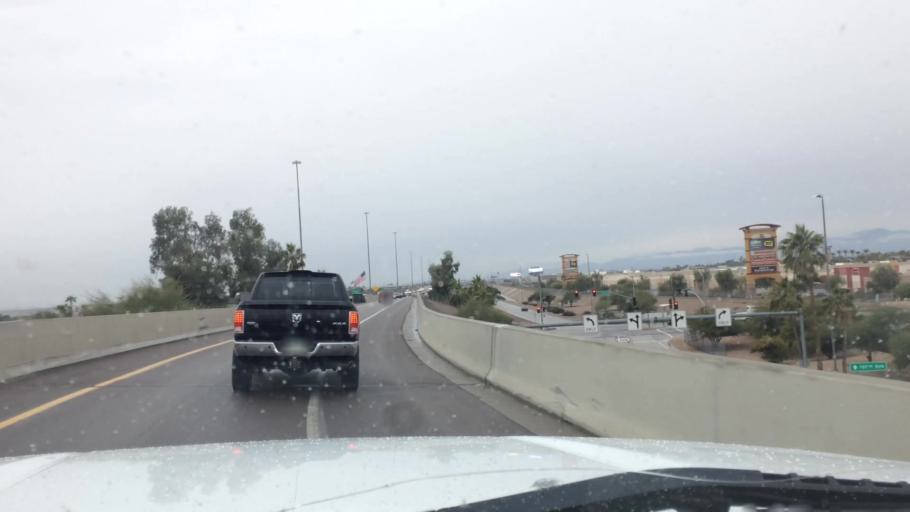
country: US
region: Arizona
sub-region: Maricopa County
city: Tolleson
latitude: 33.4621
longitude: -112.2709
